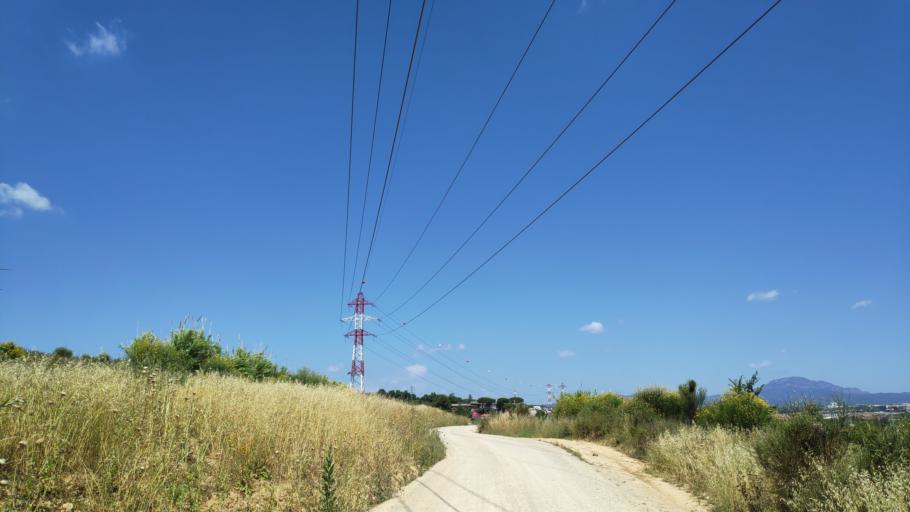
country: ES
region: Catalonia
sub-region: Provincia de Barcelona
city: Barbera del Valles
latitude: 41.5116
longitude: 2.1009
